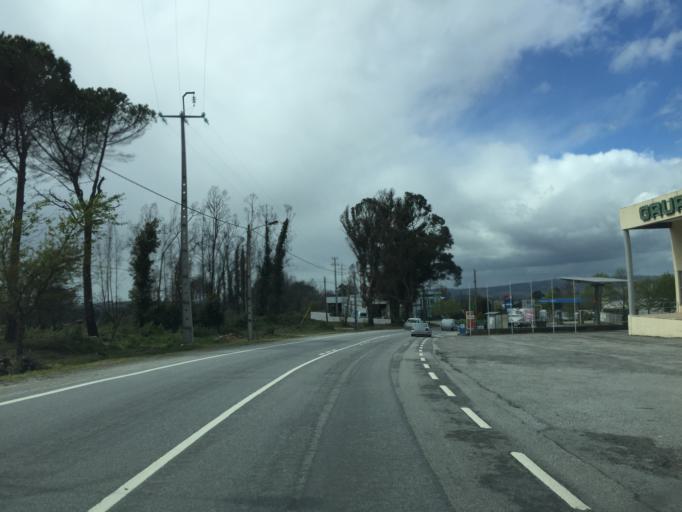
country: PT
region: Guarda
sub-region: Seia
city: Seia
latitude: 40.5092
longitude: -7.6264
